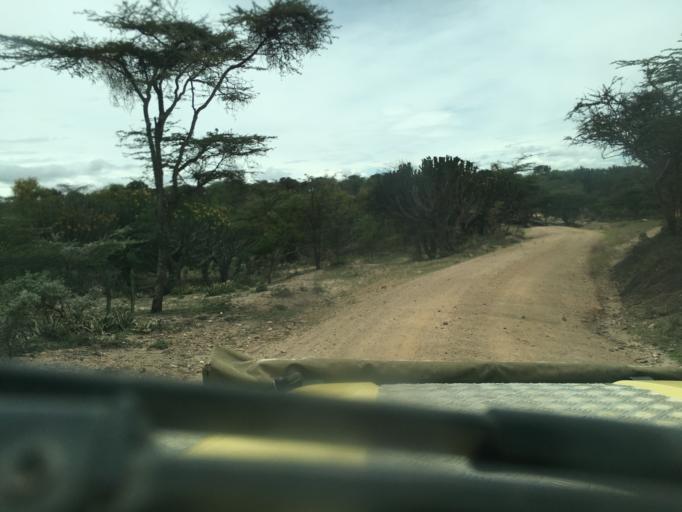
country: KE
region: Kajiado
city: Magadi
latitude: -2.0294
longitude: 35.5455
